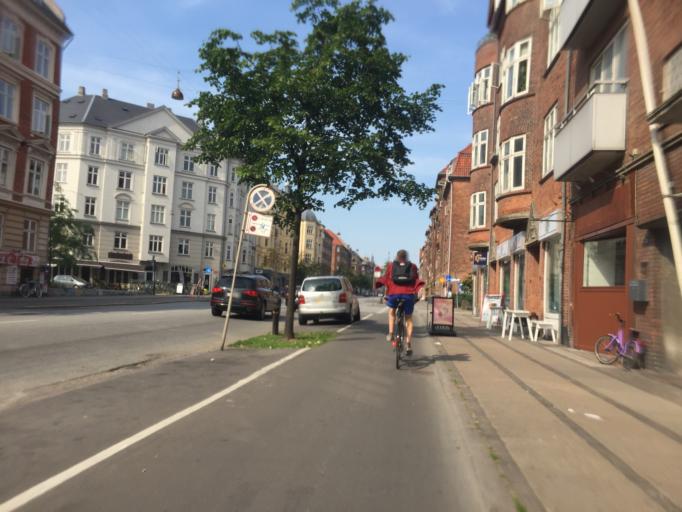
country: DK
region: Capital Region
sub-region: Frederiksberg Kommune
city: Frederiksberg
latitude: 55.6963
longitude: 12.5512
